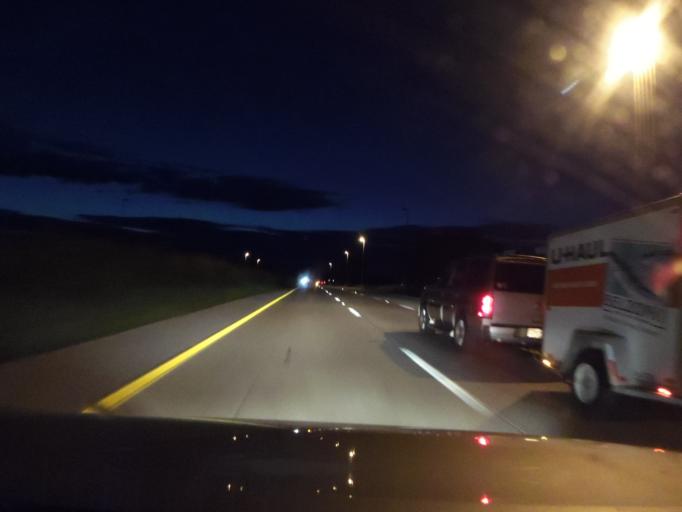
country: US
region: Kentucky
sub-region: Christian County
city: Fort Campbell North
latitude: 36.7466
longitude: -87.5153
